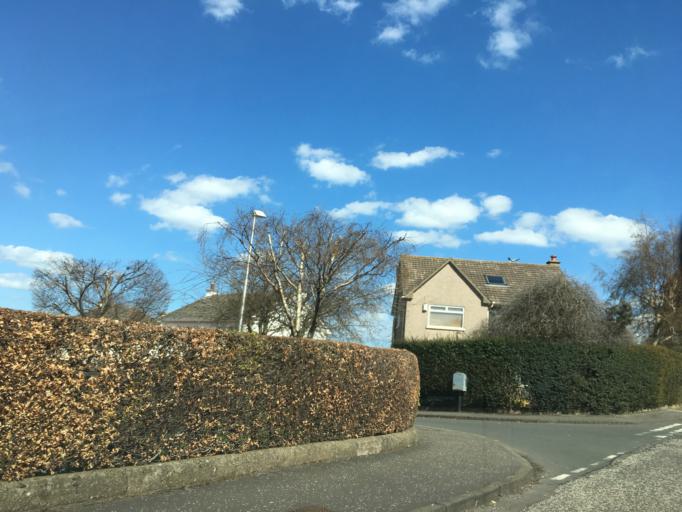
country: GB
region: Scotland
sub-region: Edinburgh
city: Colinton
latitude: 55.9029
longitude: -3.2133
